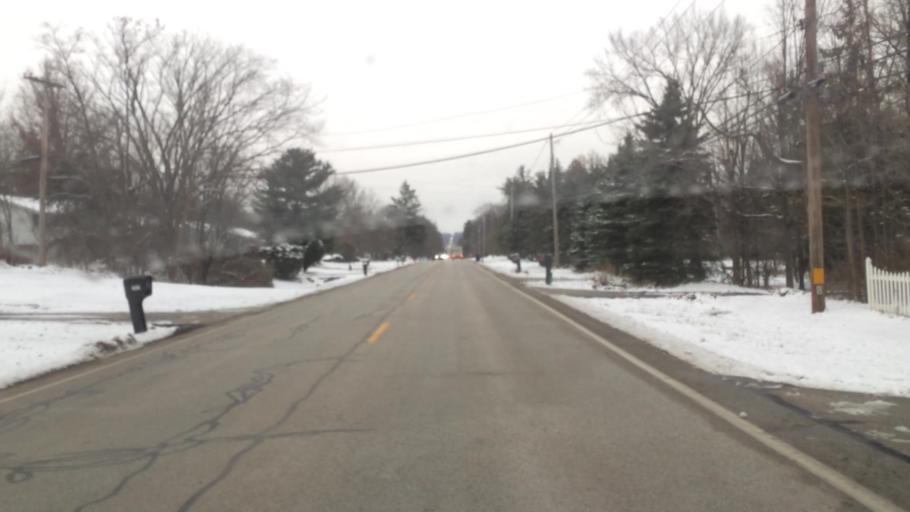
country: US
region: Ohio
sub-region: Cuyahoga County
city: Strongsville
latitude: 41.2940
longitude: -81.7853
